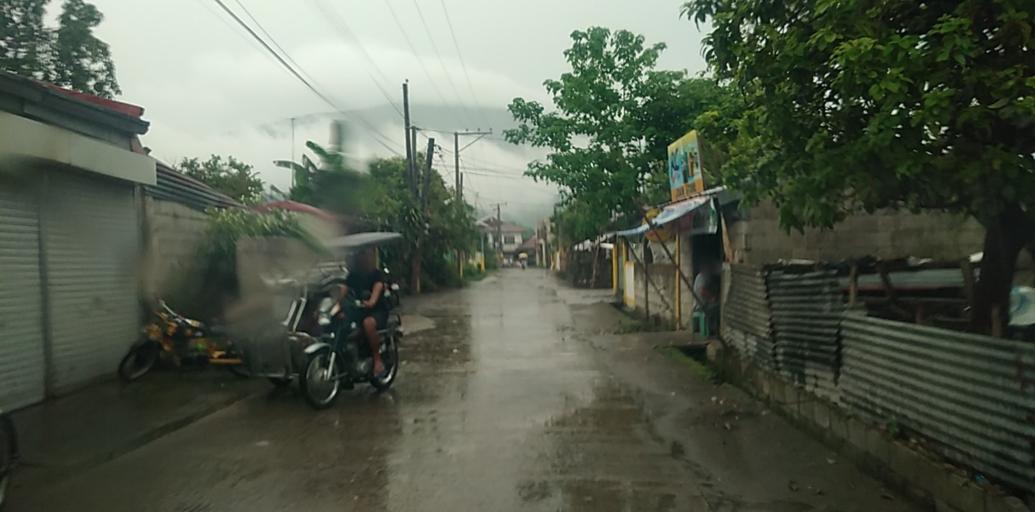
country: PH
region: Central Luzon
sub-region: Province of Pampanga
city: Anao
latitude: 15.1561
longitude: 120.7231
